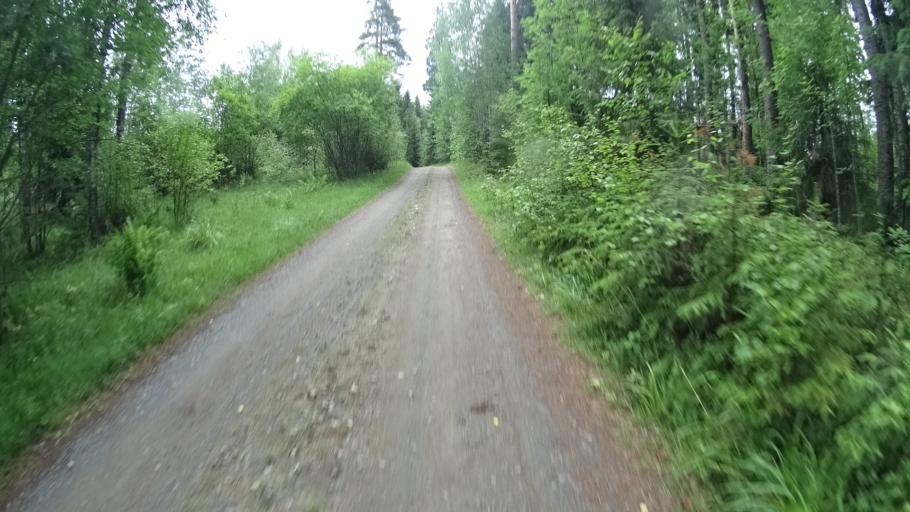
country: FI
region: Uusimaa
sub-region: Helsinki
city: Karkkila
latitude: 60.5796
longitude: 24.2748
